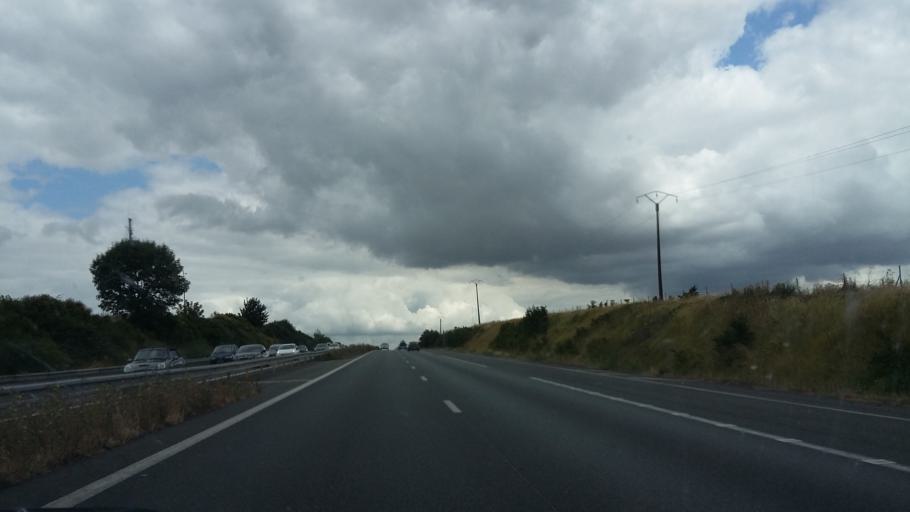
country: FR
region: Poitou-Charentes
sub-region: Departement de la Vienne
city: Antran
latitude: 46.8905
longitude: 0.5188
